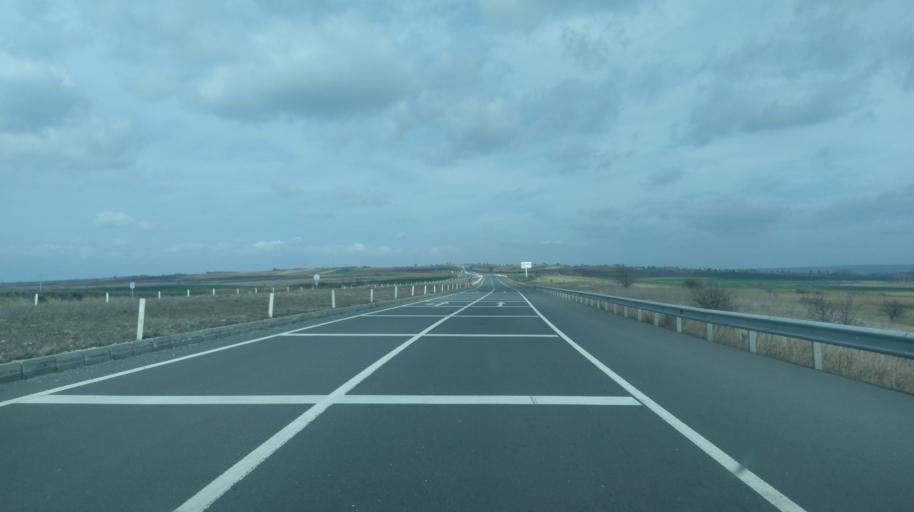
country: TR
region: Edirne
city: Hamidiye
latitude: 41.0408
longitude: 26.6343
